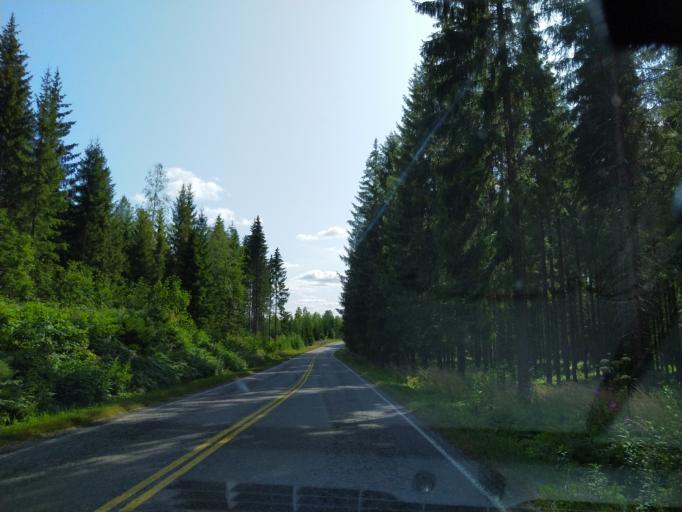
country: FI
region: Uusimaa
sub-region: Helsinki
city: Karkkila
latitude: 60.6078
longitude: 24.2710
